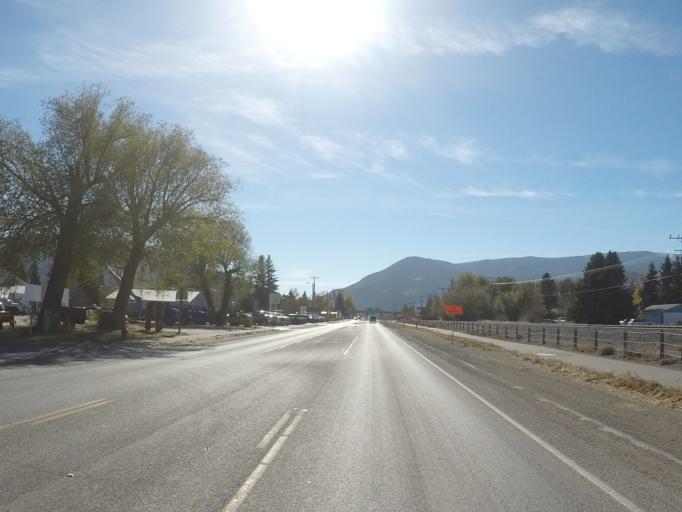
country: US
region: Montana
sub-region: Park County
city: Livingston
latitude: 45.6503
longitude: -110.5723
